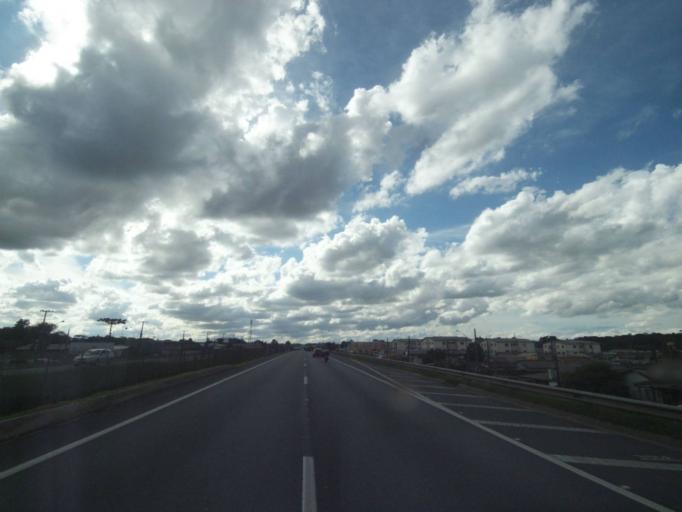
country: BR
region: Parana
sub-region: Piraquara
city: Piraquara
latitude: -25.5247
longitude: -49.0978
